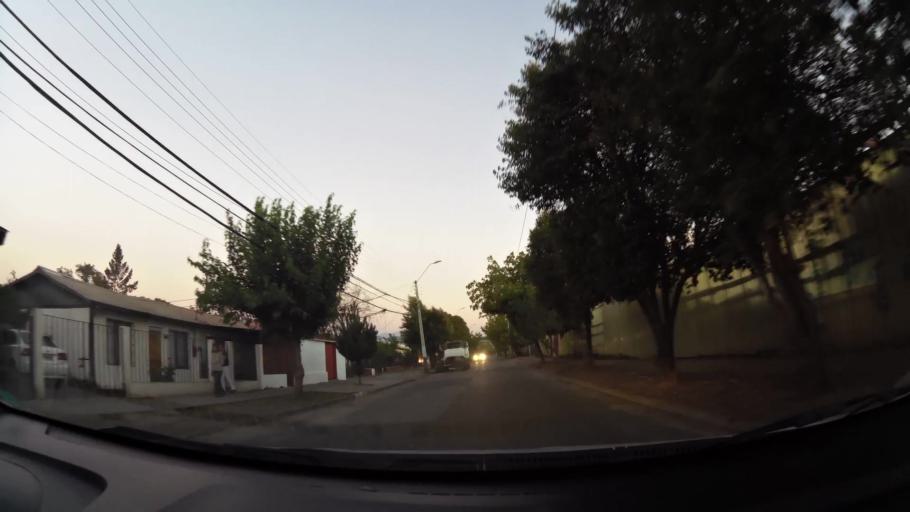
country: CL
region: O'Higgins
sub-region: Provincia de Cachapoal
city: Rancagua
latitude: -34.1828
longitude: -70.7325
